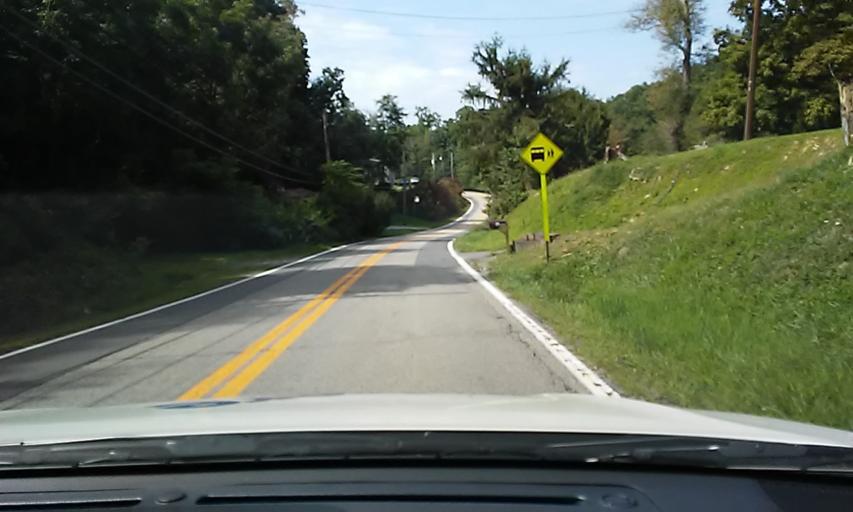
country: US
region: West Virginia
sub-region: Marion County
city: Barrackville
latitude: 39.5671
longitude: -80.1103
